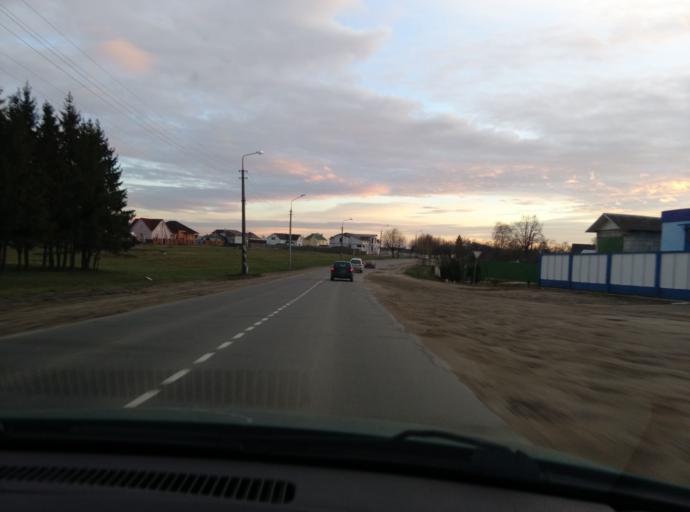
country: BY
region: Minsk
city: Horad Barysaw
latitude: 54.2651
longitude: 28.5007
